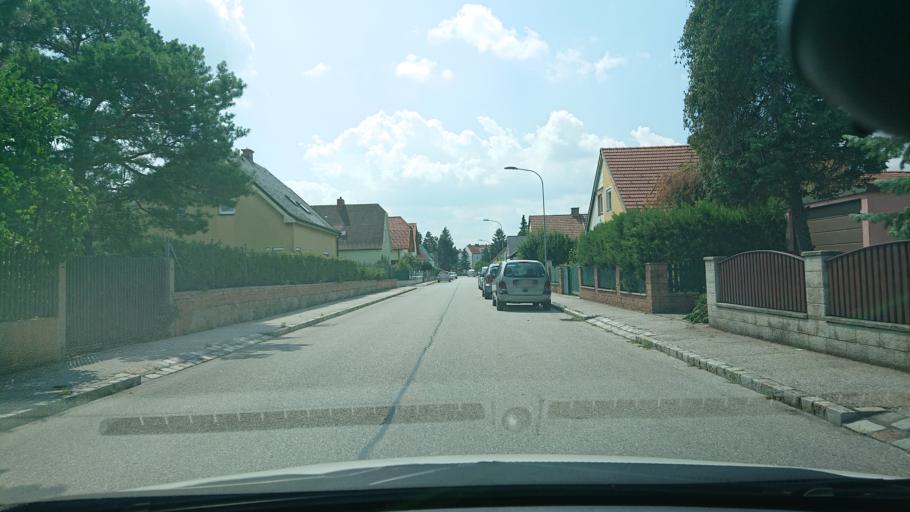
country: AT
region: Lower Austria
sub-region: Politischer Bezirk Baden
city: Leobersdorf
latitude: 47.9319
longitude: 16.2133
